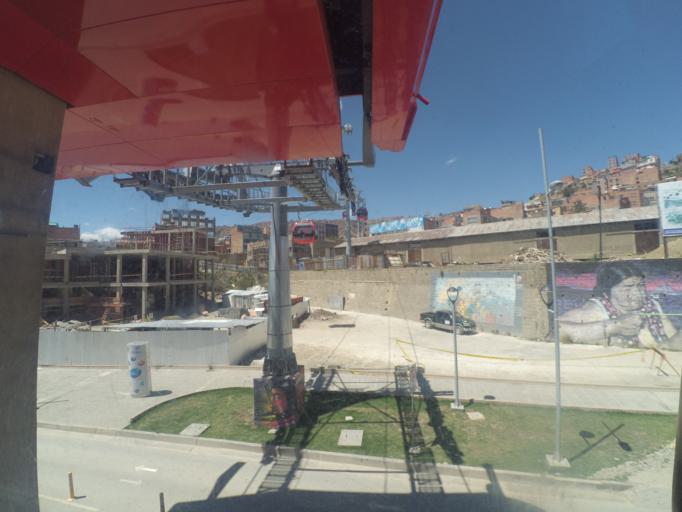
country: BO
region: La Paz
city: La Paz
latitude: -16.4916
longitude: -68.1449
